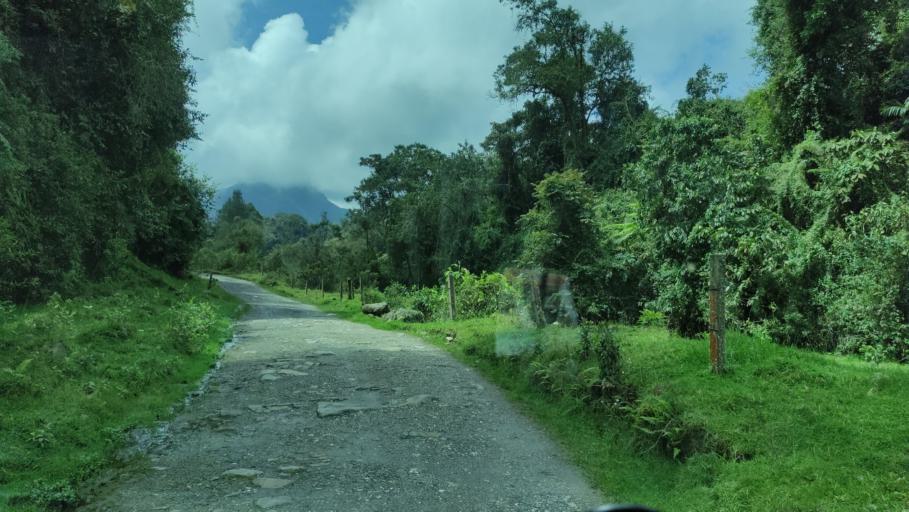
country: CO
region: Caldas
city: Villamaria
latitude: 4.9869
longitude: -75.4427
